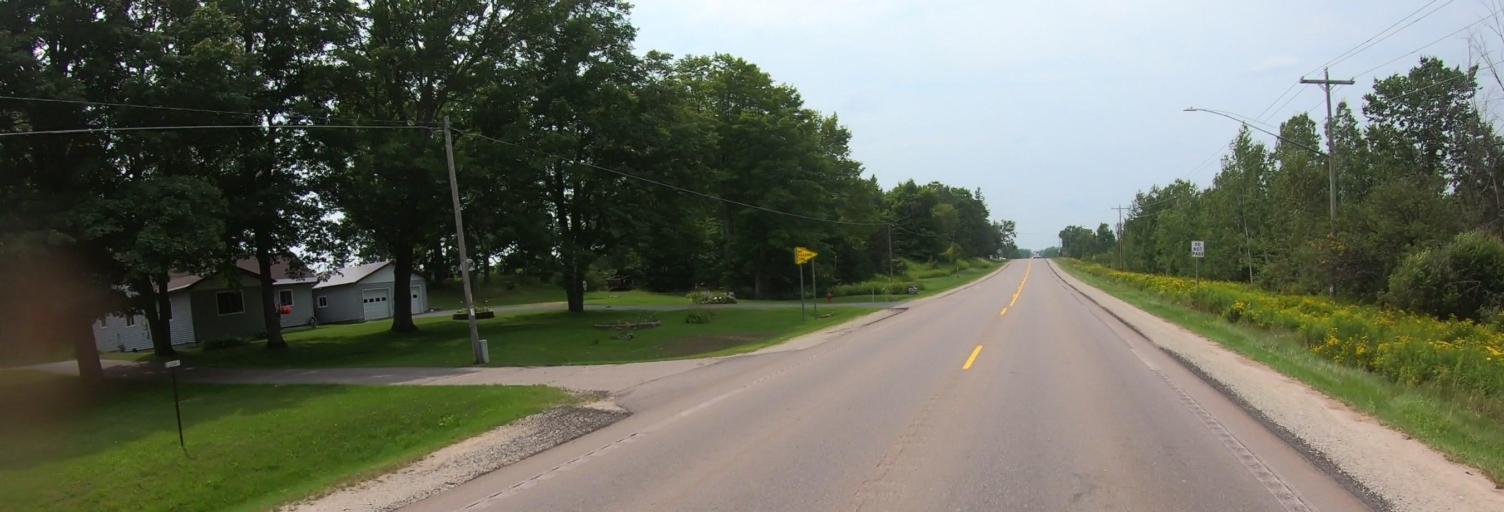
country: US
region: Michigan
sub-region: Alger County
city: Munising
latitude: 46.3476
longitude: -86.9354
